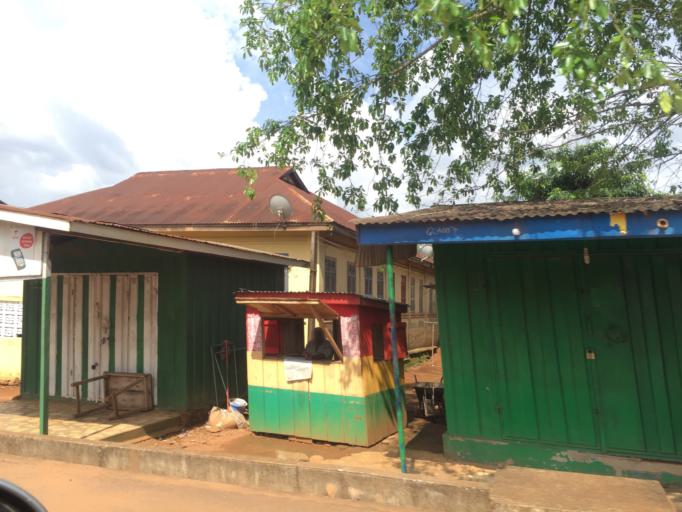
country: GH
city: Mpraeso
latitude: 6.5867
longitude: -0.7365
